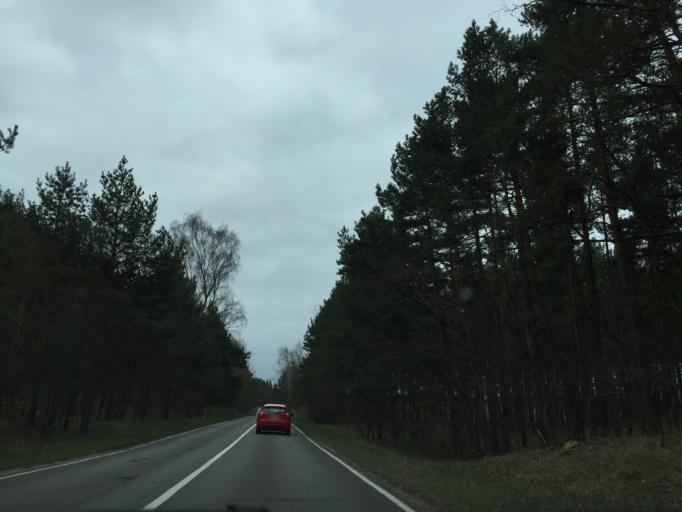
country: LT
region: Klaipedos apskritis
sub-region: Klaipeda
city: Klaipeda
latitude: 55.6596
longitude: 21.1164
